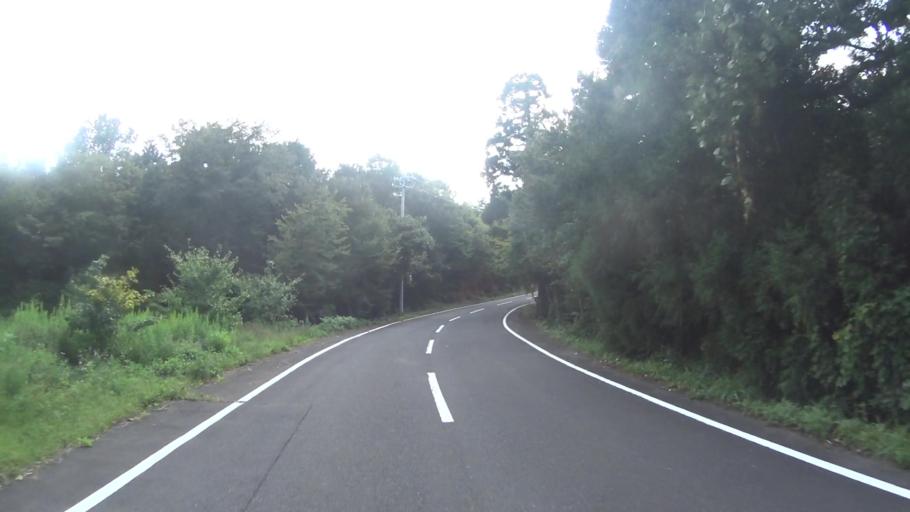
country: JP
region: Kyoto
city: Miyazu
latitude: 35.7428
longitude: 135.1736
